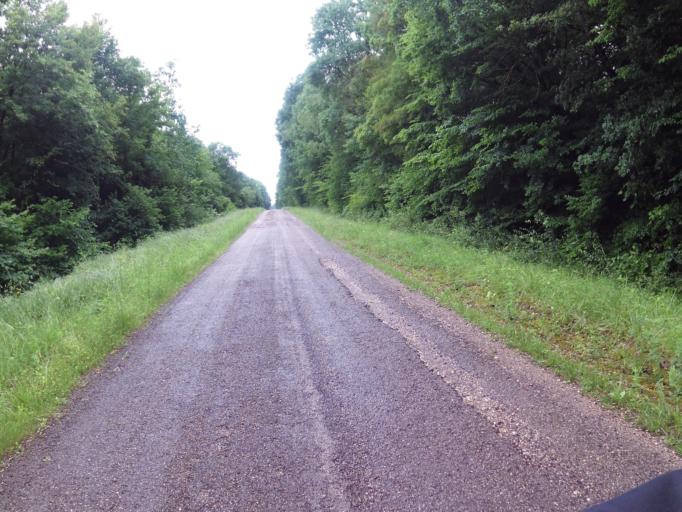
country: FR
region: Champagne-Ardenne
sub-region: Departement de la Marne
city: Sermaize-les-Bains
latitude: 48.7614
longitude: 4.9484
